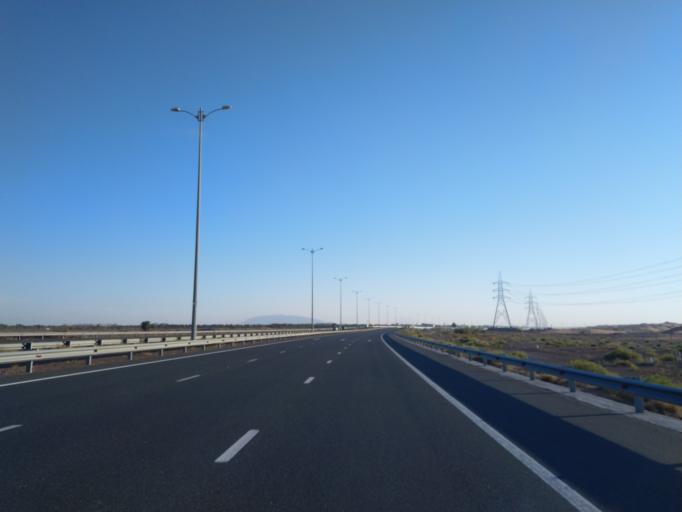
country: OM
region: Al Buraimi
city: Al Buraymi
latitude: 24.3788
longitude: 55.7977
